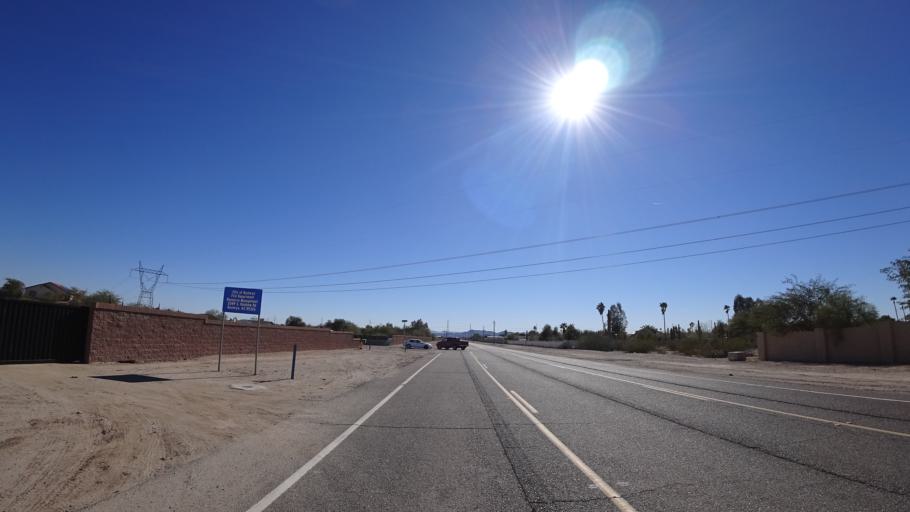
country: US
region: Arizona
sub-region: Maricopa County
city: Buckeye
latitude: 33.4280
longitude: -112.5390
